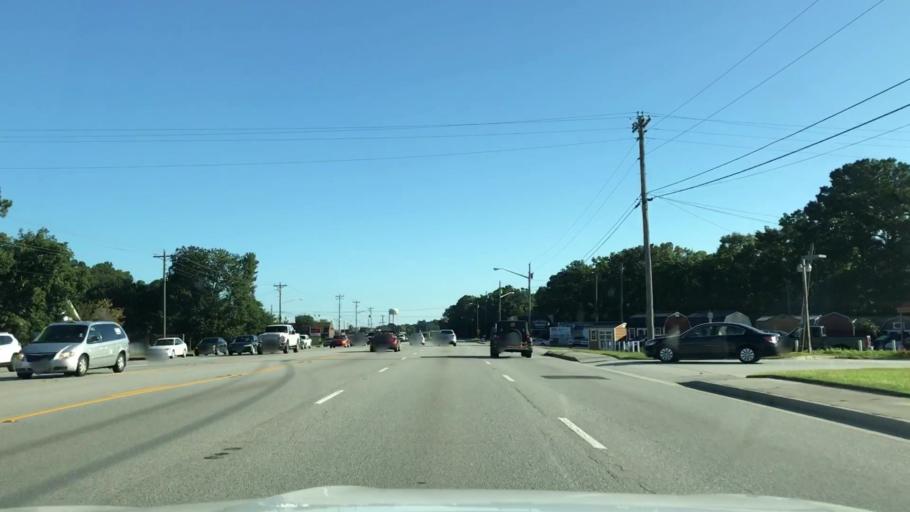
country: US
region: South Carolina
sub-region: Berkeley County
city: Goose Creek
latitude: 32.9887
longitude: -80.0402
